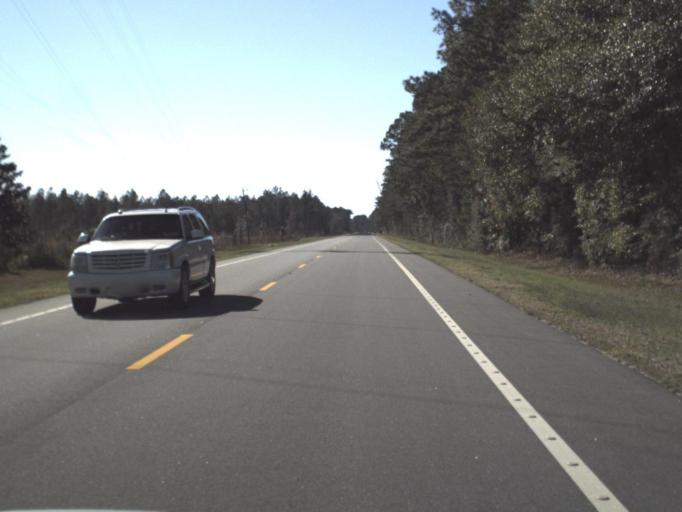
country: US
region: Florida
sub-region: Calhoun County
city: Blountstown
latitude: 30.4369
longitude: -85.2066
